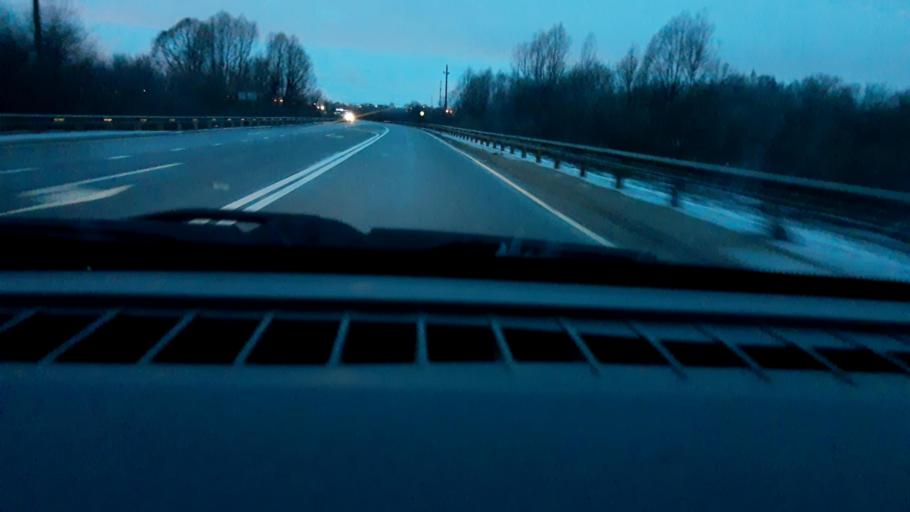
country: RU
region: Nizjnij Novgorod
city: Kstovo
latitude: 56.1227
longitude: 44.2200
